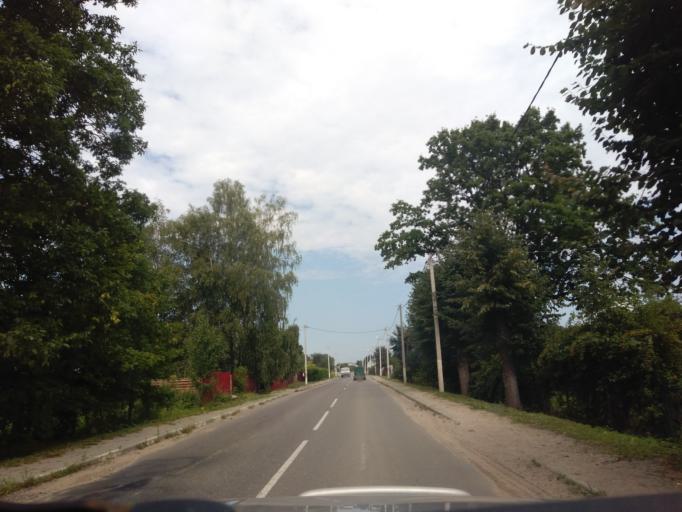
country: BY
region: Minsk
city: Khatsyezhyna
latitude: 53.9119
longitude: 27.3112
